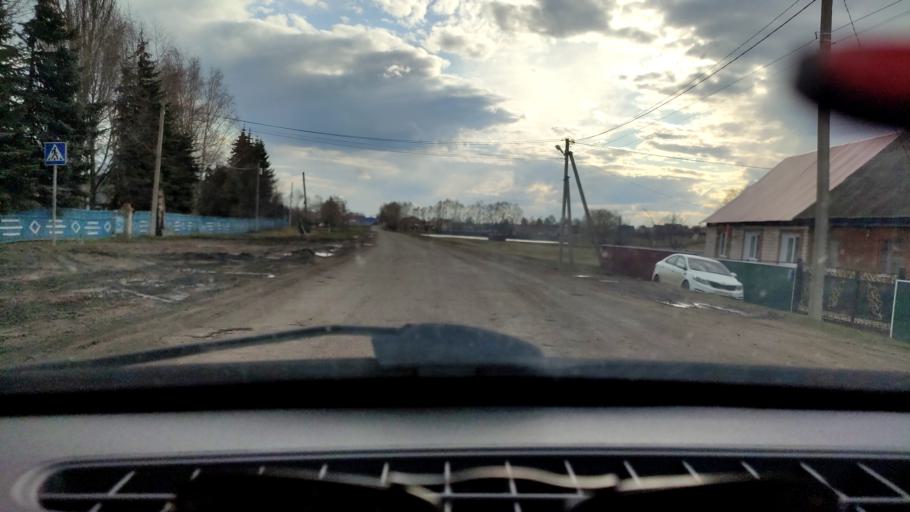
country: RU
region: Bashkortostan
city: Karmaskaly
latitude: 54.3768
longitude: 56.2056
